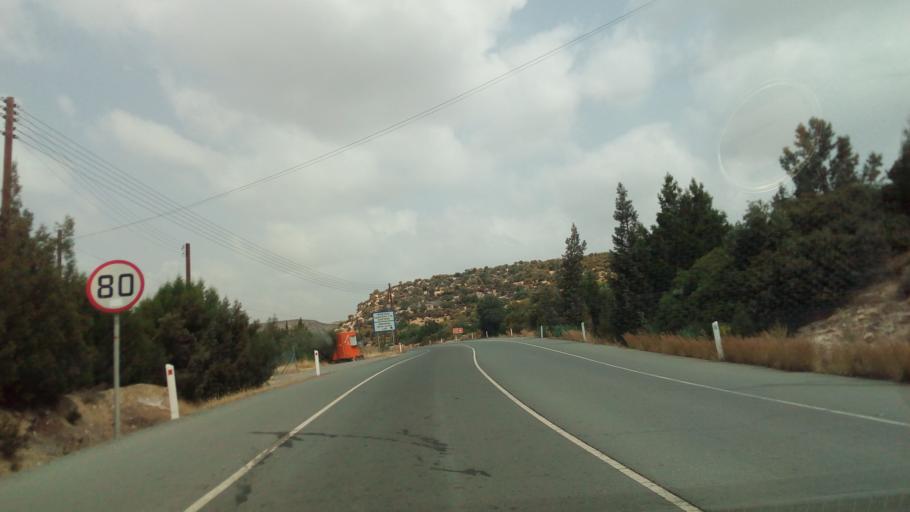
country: CY
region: Limassol
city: Pano Polemidia
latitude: 34.7184
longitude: 32.9908
